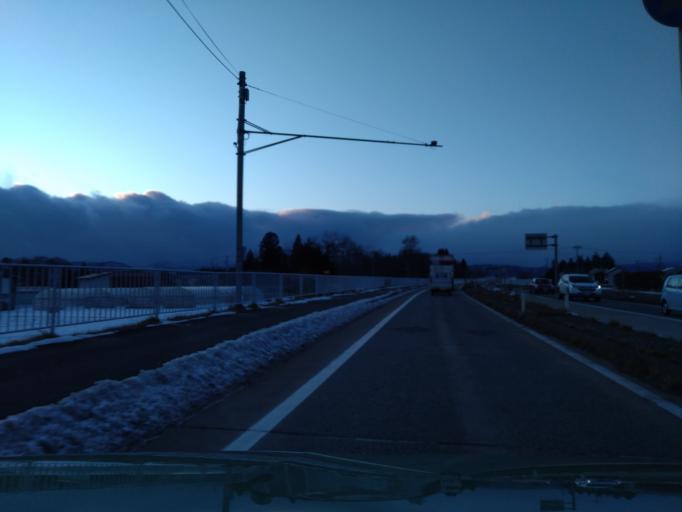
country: JP
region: Iwate
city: Shizukuishi
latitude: 39.6894
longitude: 140.9922
